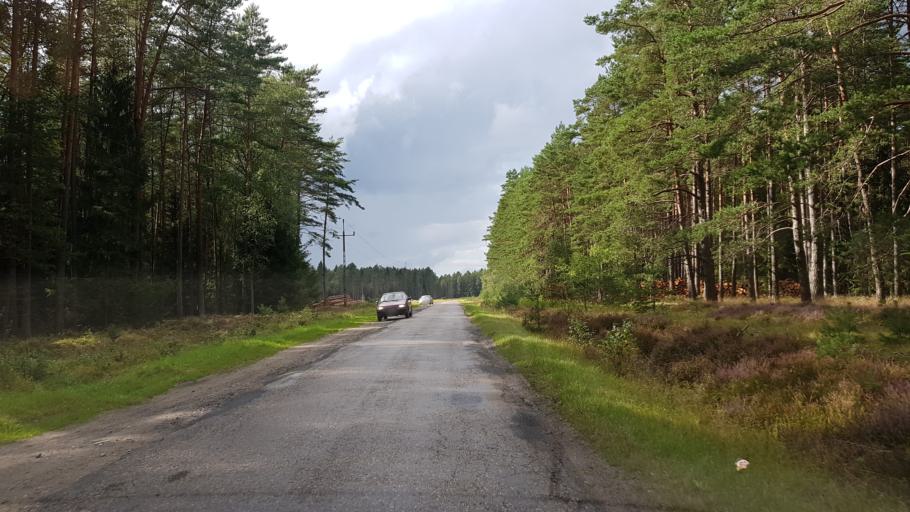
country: PL
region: West Pomeranian Voivodeship
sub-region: Powiat bialogardzki
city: Tychowo
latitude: 54.0406
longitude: 16.3258
